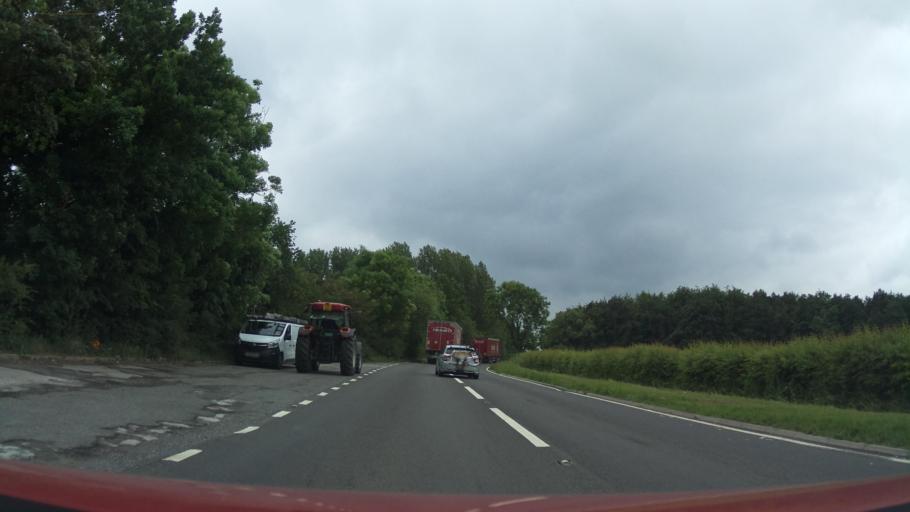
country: GB
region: England
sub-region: Staffordshire
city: Mayfield
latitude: 52.9819
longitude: -1.7485
